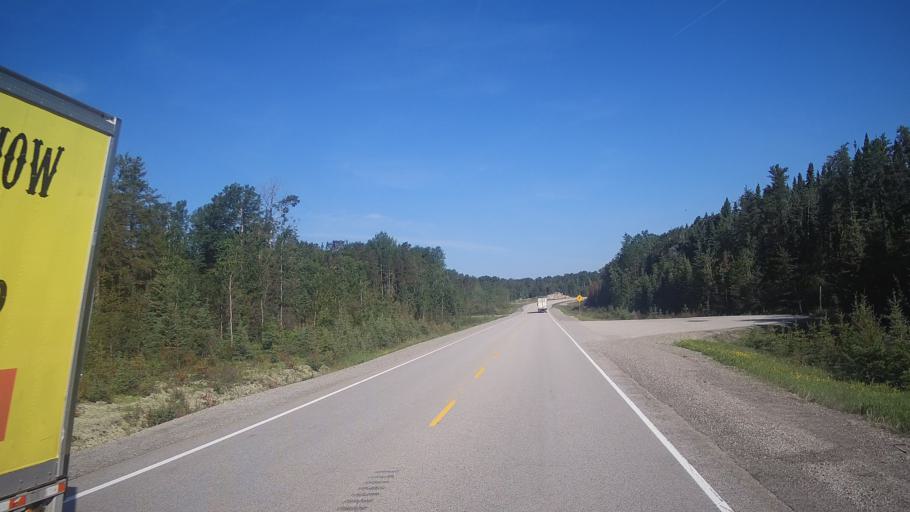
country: CA
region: Ontario
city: Dryden
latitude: 49.5712
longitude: -92.2540
